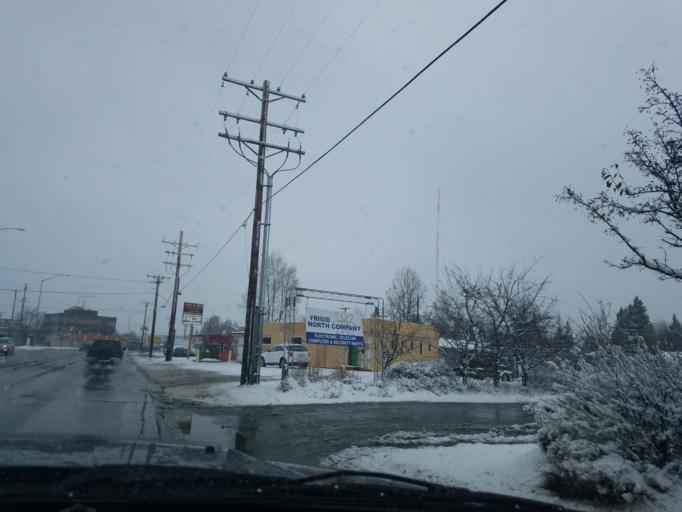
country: US
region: Alaska
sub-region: Anchorage Municipality
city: Anchorage
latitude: 61.1902
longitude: -149.9076
